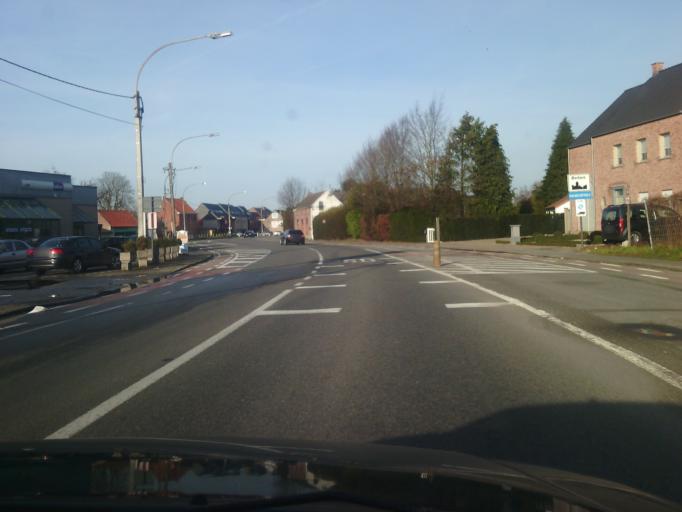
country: BE
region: Flanders
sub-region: Provincie Oost-Vlaanderen
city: Berlare
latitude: 51.0086
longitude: 4.0090
